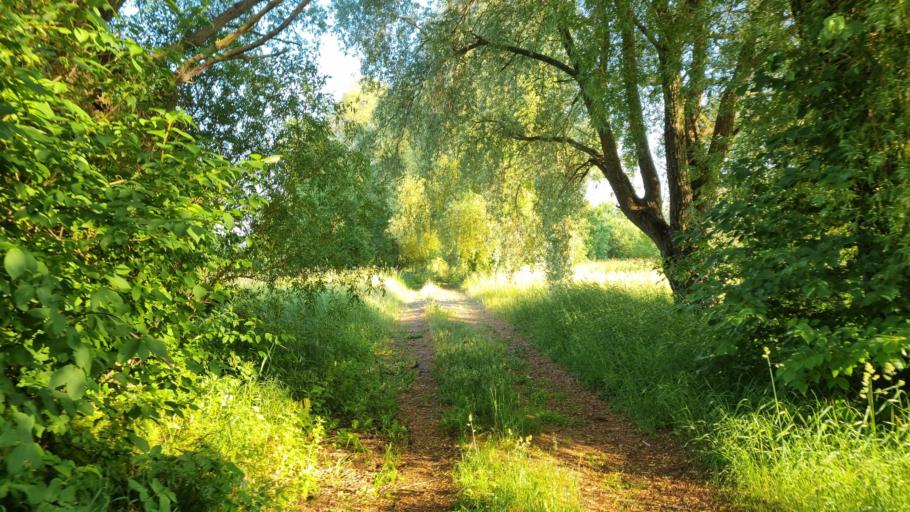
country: LV
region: Ventspils
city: Ventspils
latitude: 57.3739
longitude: 21.5992
